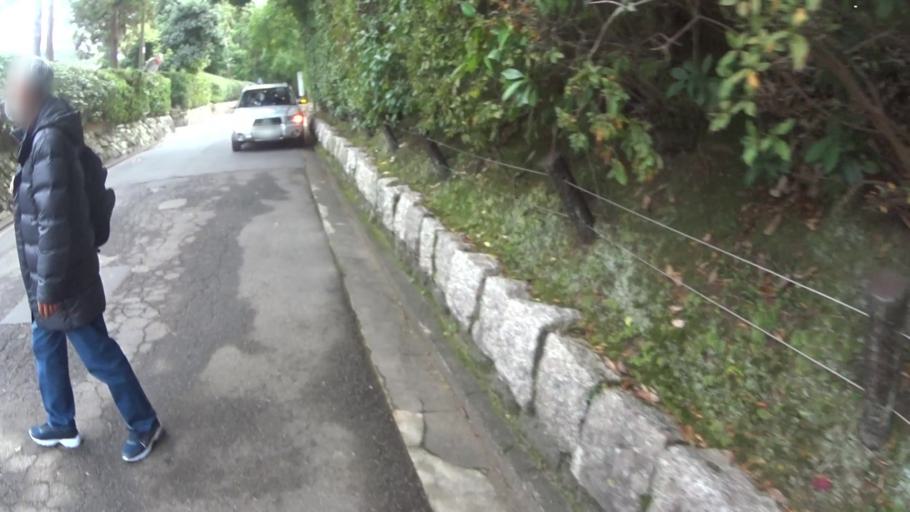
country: JP
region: Kyoto
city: Kyoto
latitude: 34.9808
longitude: 135.7778
